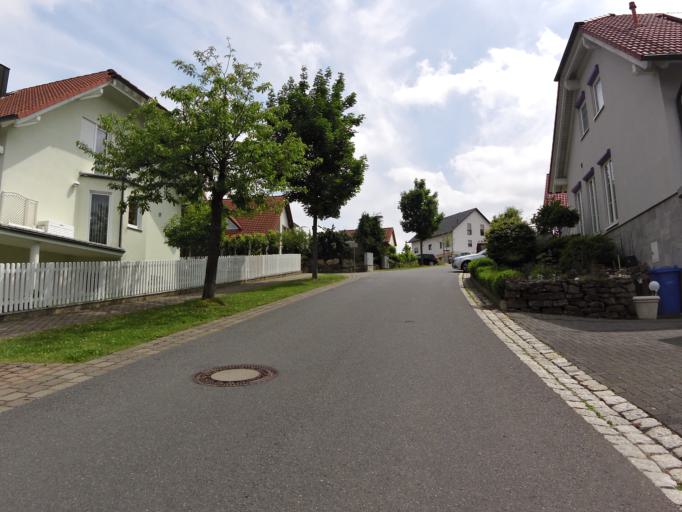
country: DE
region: Bavaria
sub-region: Regierungsbezirk Unterfranken
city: Waldbrunn
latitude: 49.7624
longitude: 9.8042
